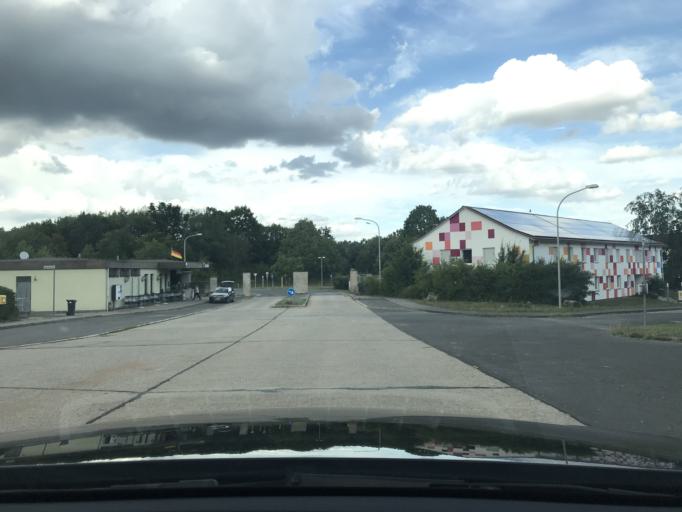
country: DE
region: Bavaria
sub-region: Regierungsbezirk Unterfranken
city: Rentweinsdorf
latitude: 50.0937
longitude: 10.7735
